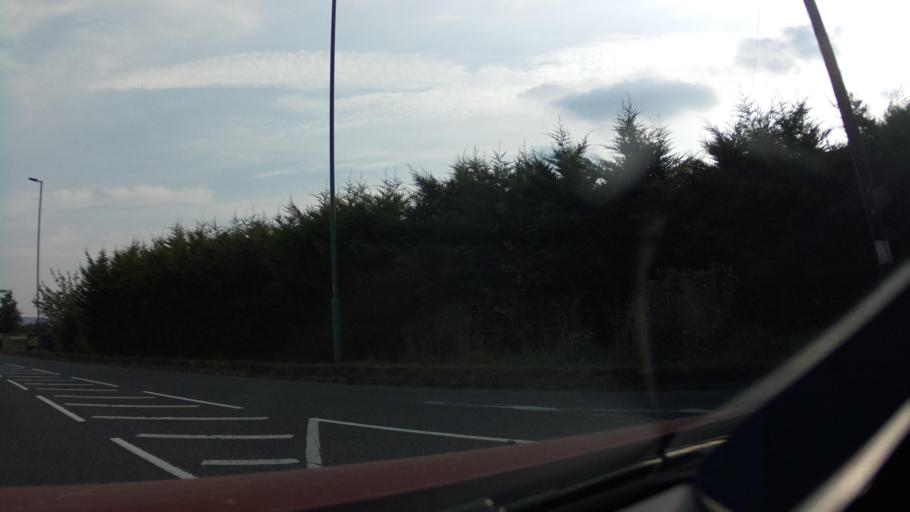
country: GB
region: England
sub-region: Gloucestershire
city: Gotherington
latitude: 51.9408
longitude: -2.0723
